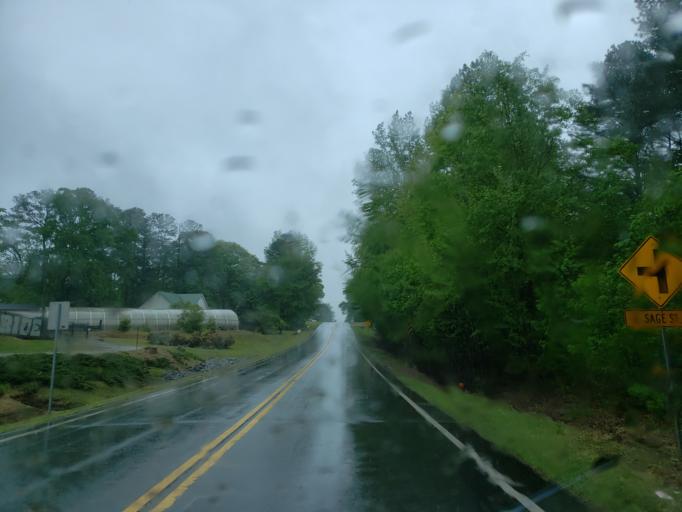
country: US
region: Georgia
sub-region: Carroll County
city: Temple
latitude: 33.7309
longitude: -85.0253
